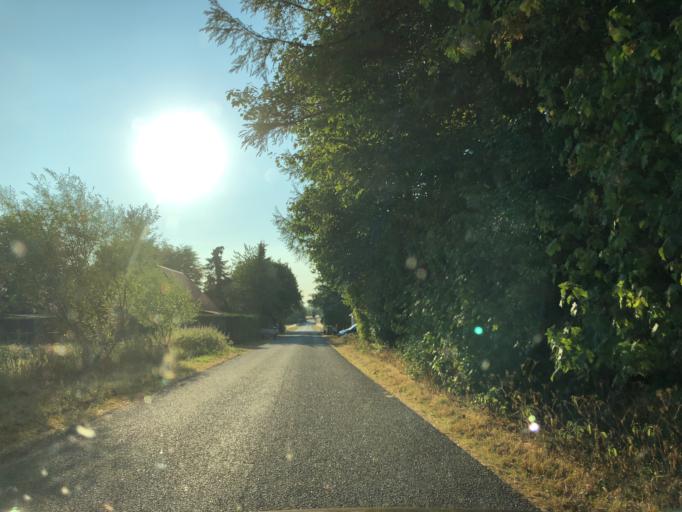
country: DK
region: Central Jutland
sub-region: Skanderborg Kommune
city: Skanderborg
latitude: 56.0877
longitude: 9.8967
